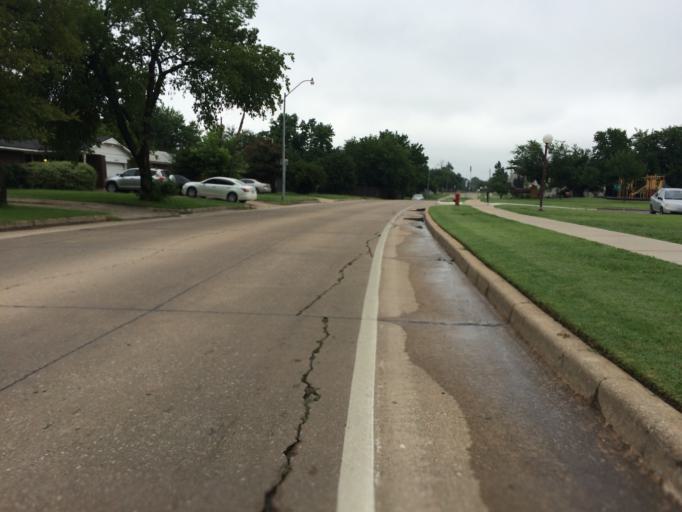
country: US
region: Oklahoma
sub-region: Cleveland County
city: Norman
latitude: 35.2061
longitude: -97.4200
